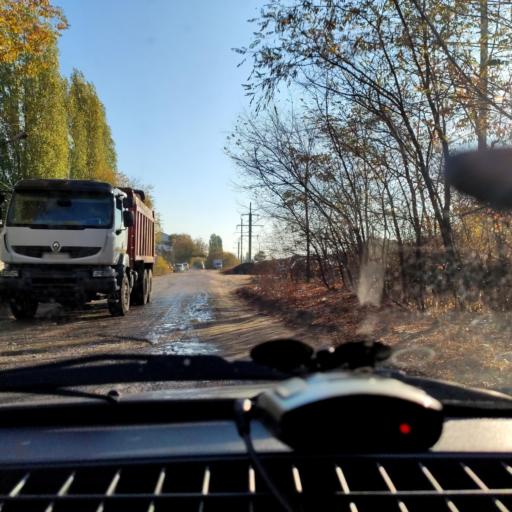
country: RU
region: Voronezj
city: Voronezh
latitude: 51.6691
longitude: 39.1441
